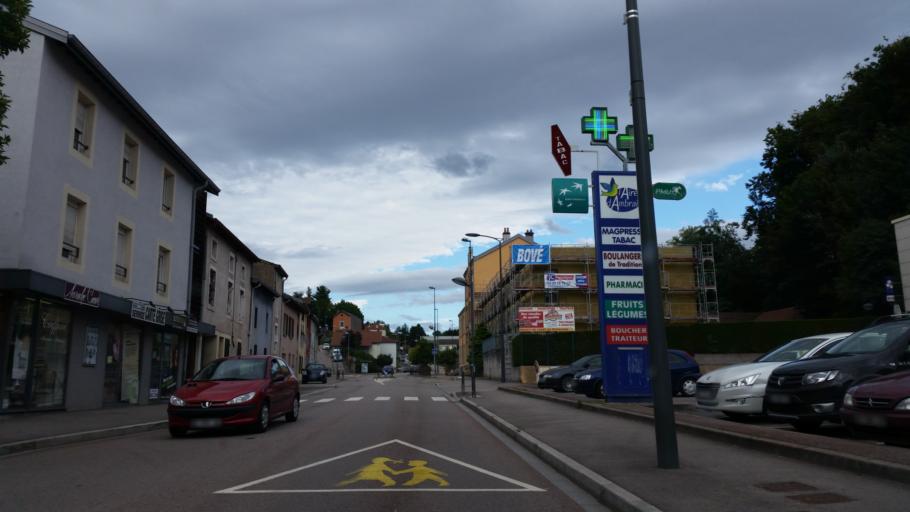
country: FR
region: Lorraine
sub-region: Departement des Vosges
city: Epinal
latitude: 48.1761
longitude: 6.4625
